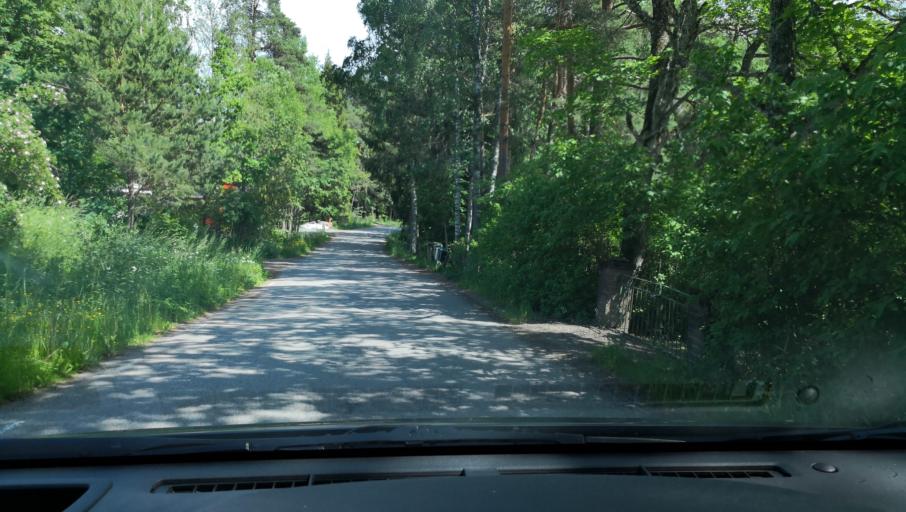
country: SE
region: Uppsala
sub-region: Uppsala Kommun
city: Alsike
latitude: 59.7044
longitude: 17.6826
